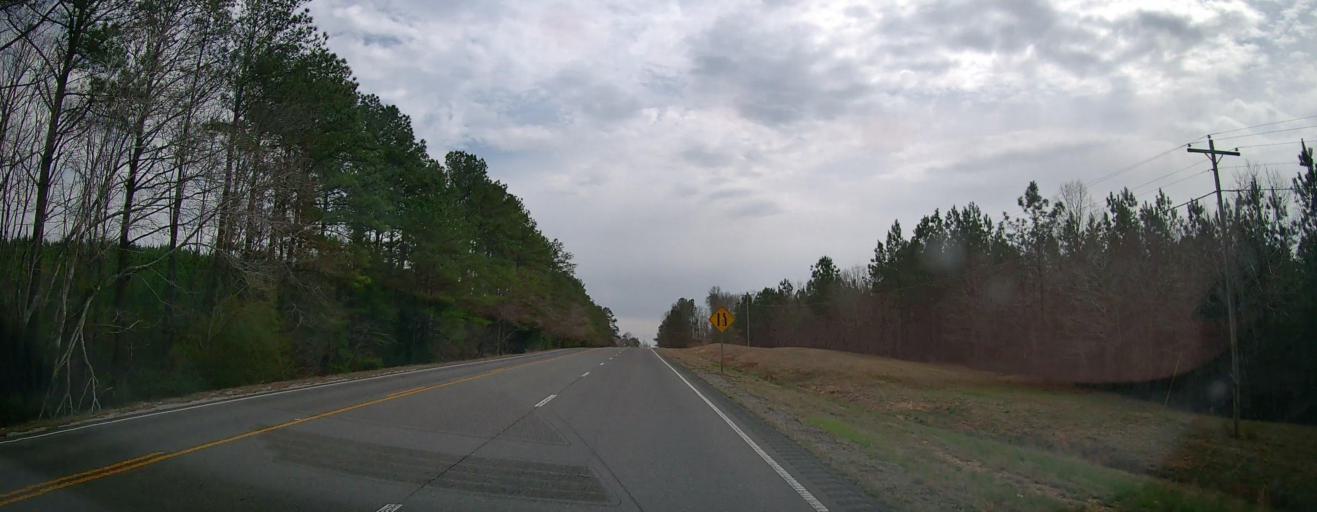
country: US
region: Alabama
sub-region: Marion County
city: Hamilton
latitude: 34.0577
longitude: -87.9672
